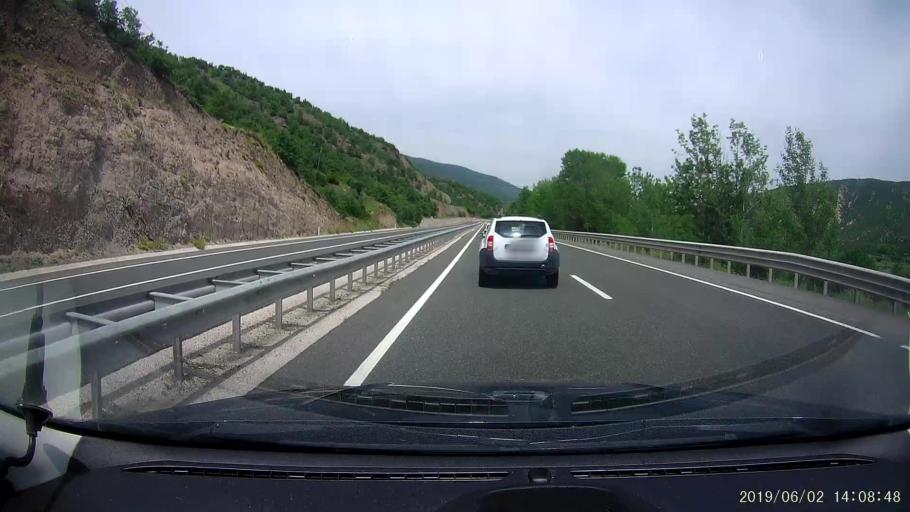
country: TR
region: Cankiri
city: Ilgaz
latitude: 40.8876
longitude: 33.7324
